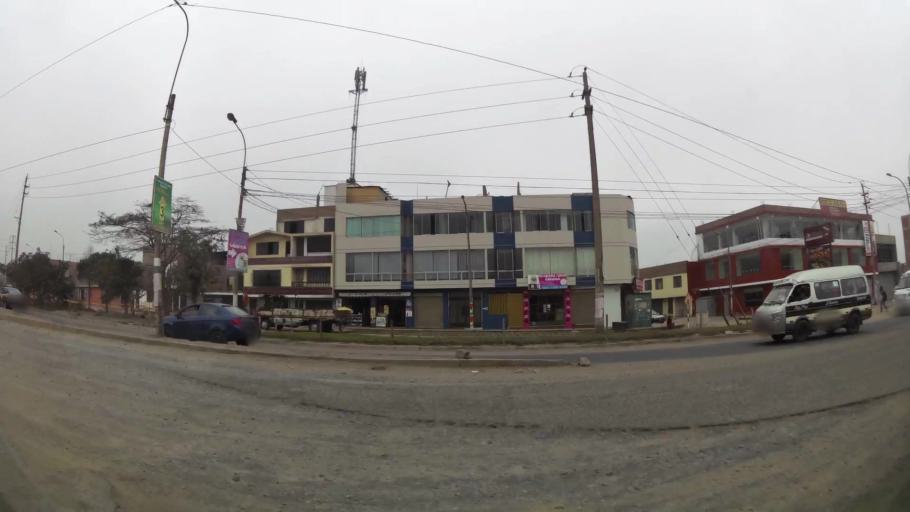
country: PE
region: Lima
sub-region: Lima
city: Urb. Santo Domingo
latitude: -11.8914
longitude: -77.0446
